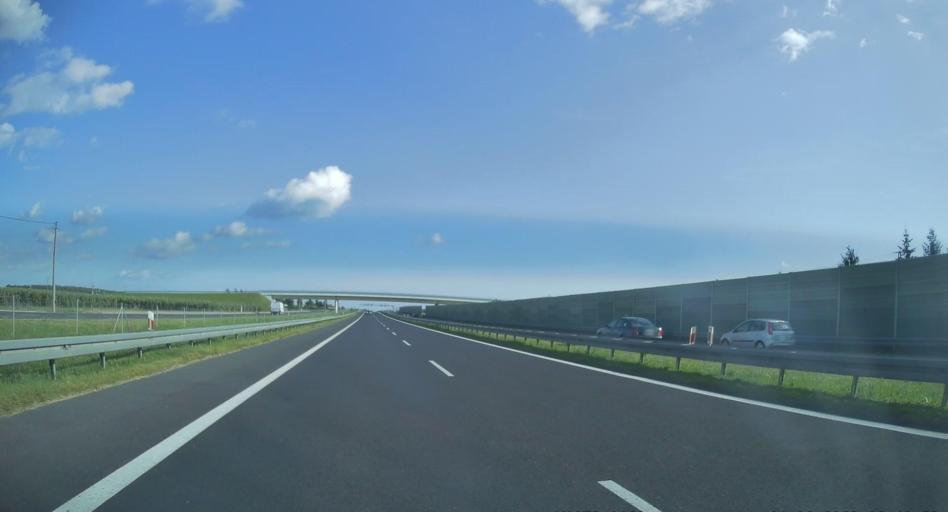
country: PL
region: Masovian Voivodeship
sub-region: Powiat bialobrzeski
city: Promna
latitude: 51.7104
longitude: 20.9256
